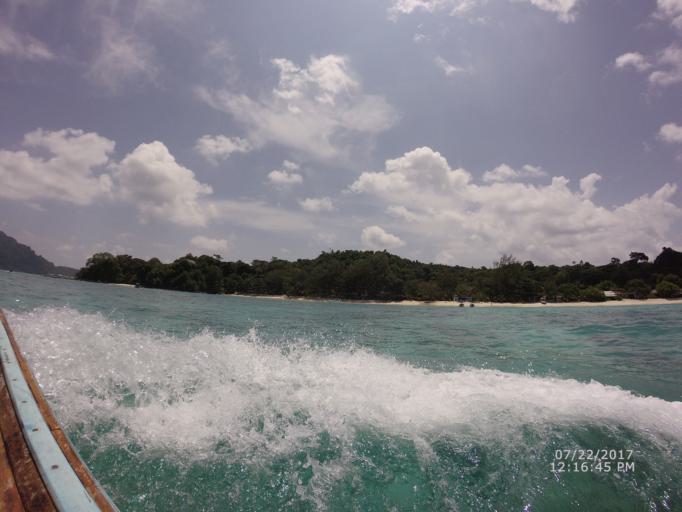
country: TH
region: Krabi
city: Saladan
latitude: 7.7285
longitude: 98.7845
